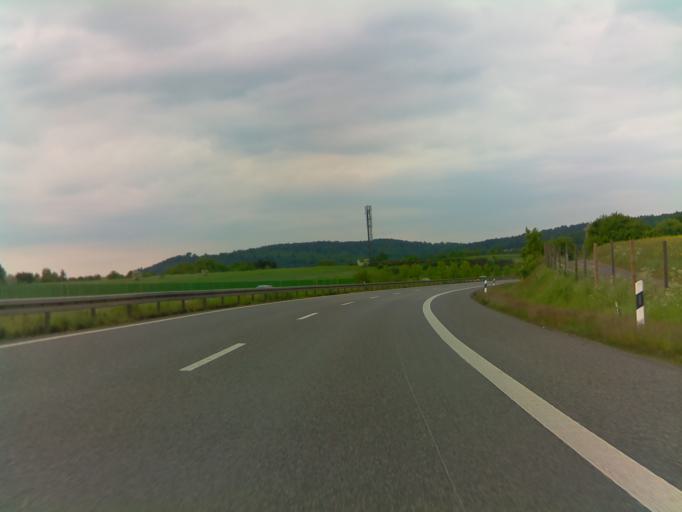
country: DE
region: Hesse
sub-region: Regierungsbezirk Giessen
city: Fronhausen
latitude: 50.7164
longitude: 8.7288
